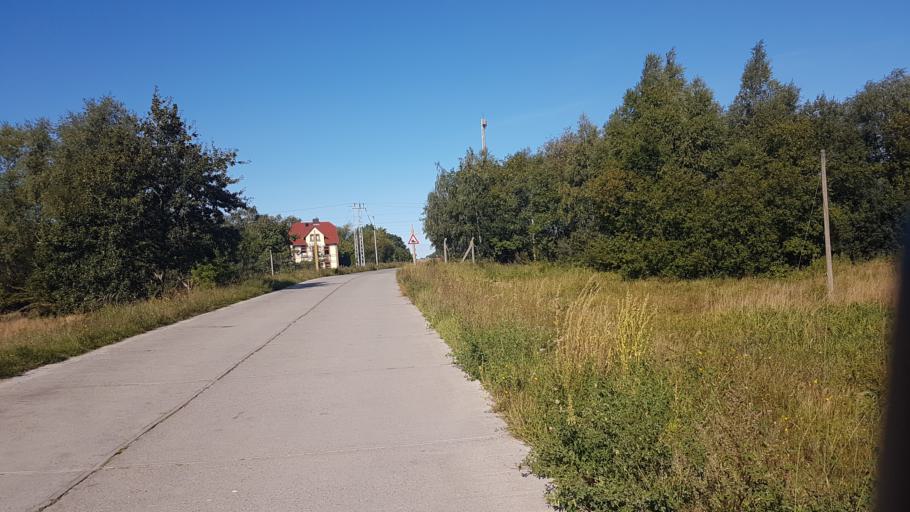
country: DE
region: Mecklenburg-Vorpommern
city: Sagard
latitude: 54.5026
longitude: 13.5323
